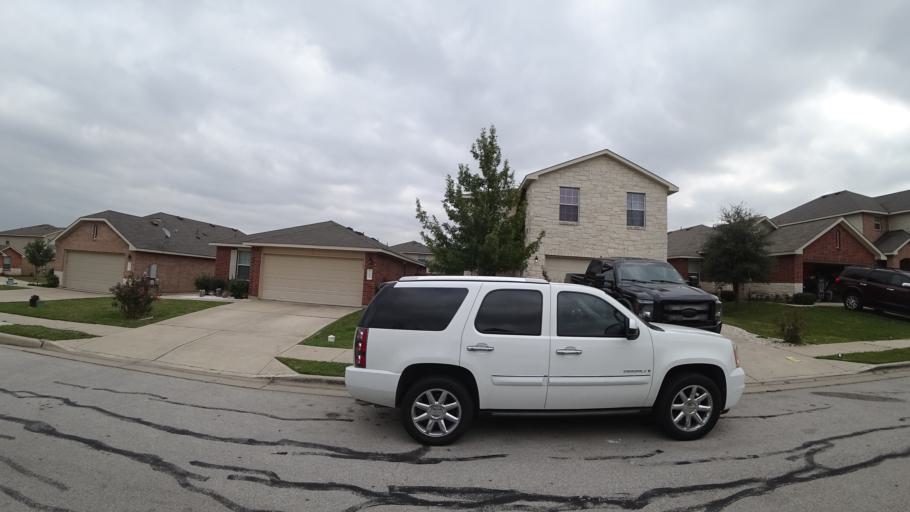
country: US
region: Texas
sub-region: Travis County
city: Pflugerville
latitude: 30.3913
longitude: -97.6173
